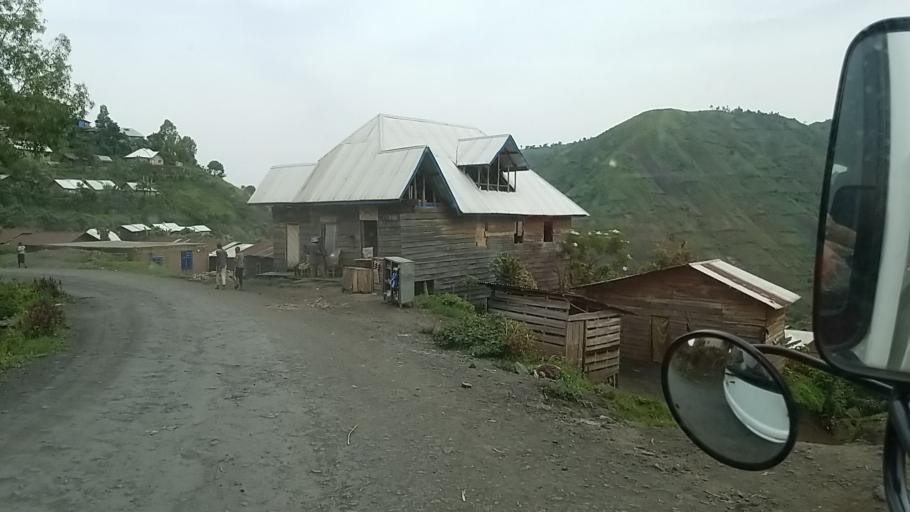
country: CD
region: Nord Kivu
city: Sake
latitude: -1.7599
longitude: 28.9868
